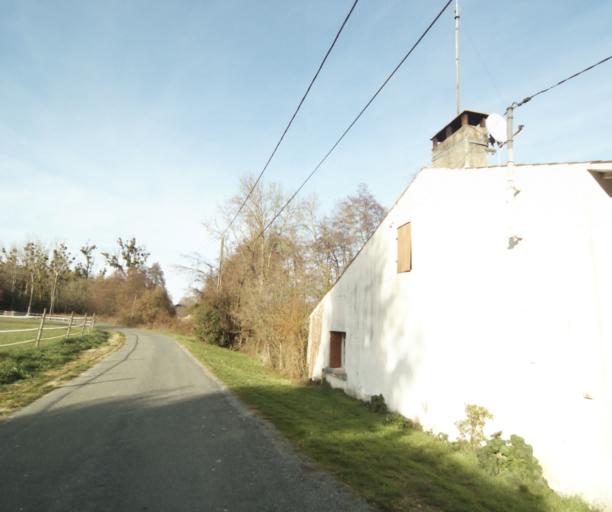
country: FR
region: Poitou-Charentes
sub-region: Departement de la Charente-Maritime
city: Chaniers
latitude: 45.7294
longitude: -0.5358
